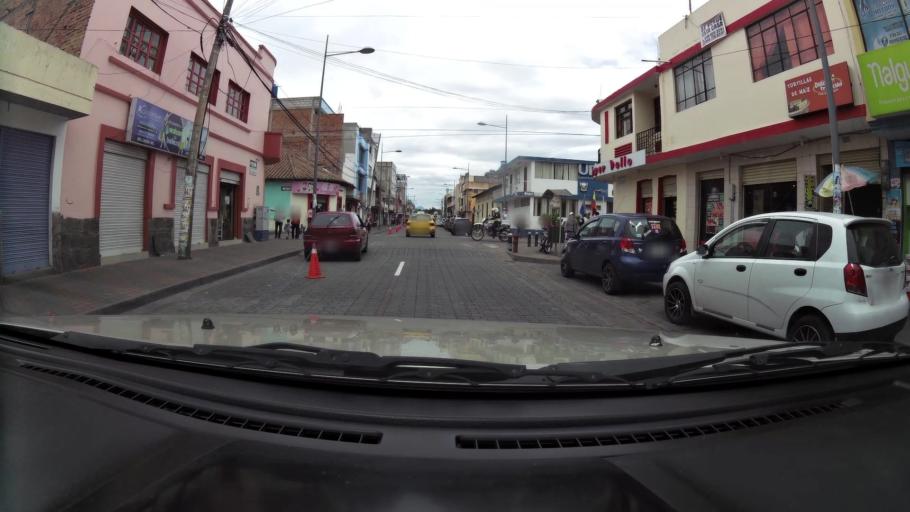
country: EC
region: Cotopaxi
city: San Miguel de Salcedo
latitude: -1.0346
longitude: -78.5881
